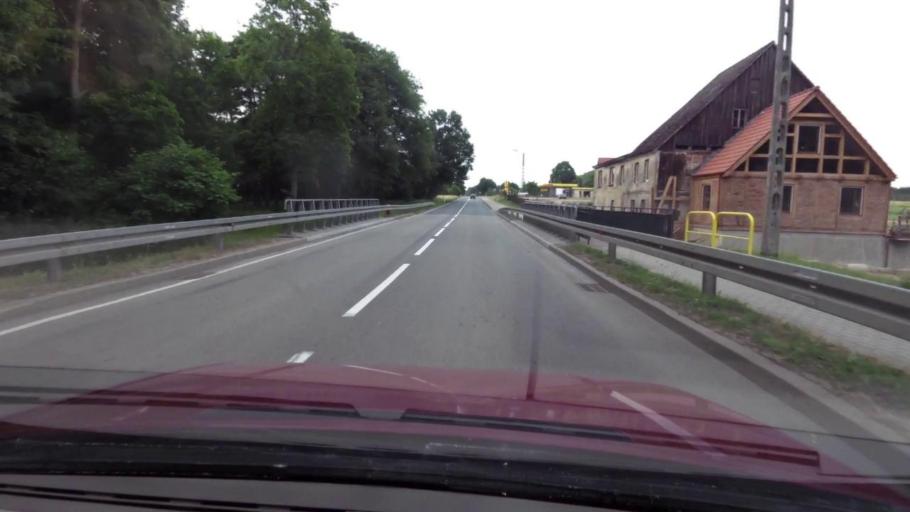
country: PL
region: Pomeranian Voivodeship
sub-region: Powiat bytowski
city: Trzebielino
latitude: 54.2083
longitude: 17.0899
